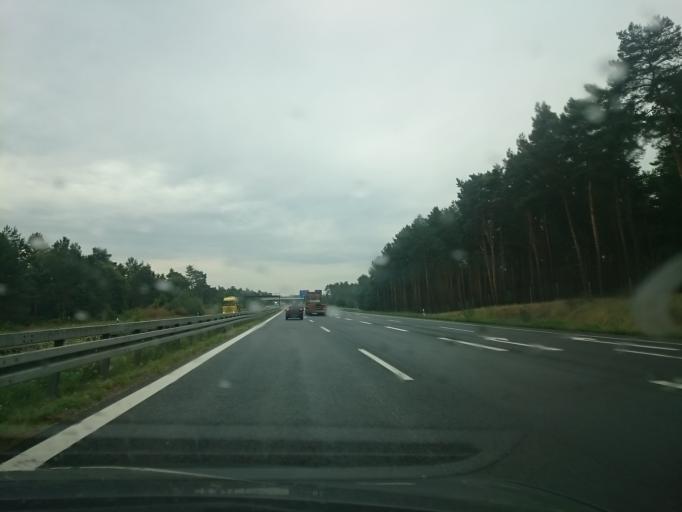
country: DE
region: Brandenburg
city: Gross Kreutz
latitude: 52.3455
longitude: 12.8156
